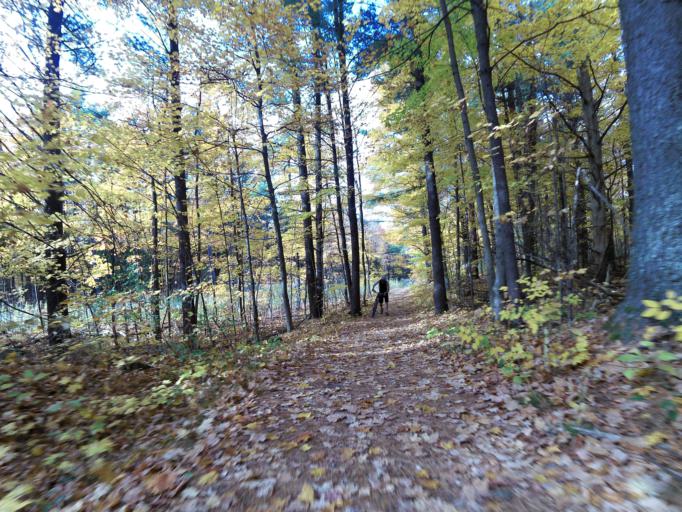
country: CA
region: Quebec
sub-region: Outaouais
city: Gatineau
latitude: 45.4828
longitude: -75.8441
